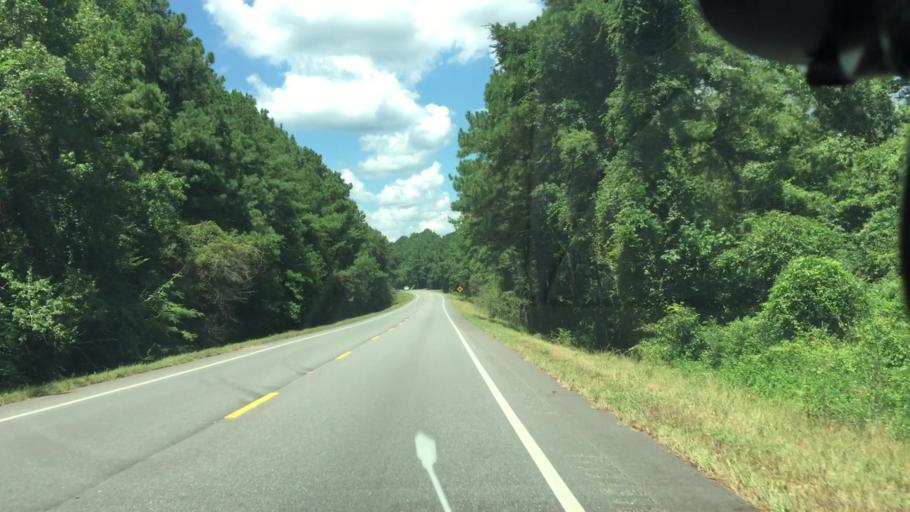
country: US
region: Alabama
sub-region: Coffee County
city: New Brockton
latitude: 31.4608
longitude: -85.8986
